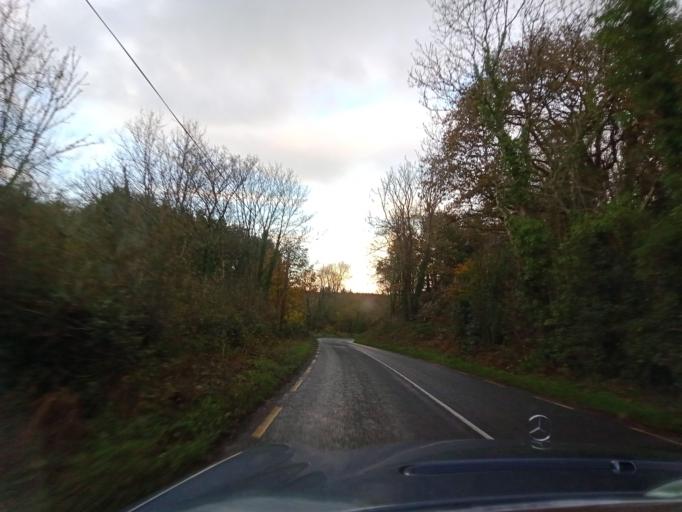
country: IE
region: Munster
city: Carrick-on-Suir
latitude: 52.4183
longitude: -7.3827
